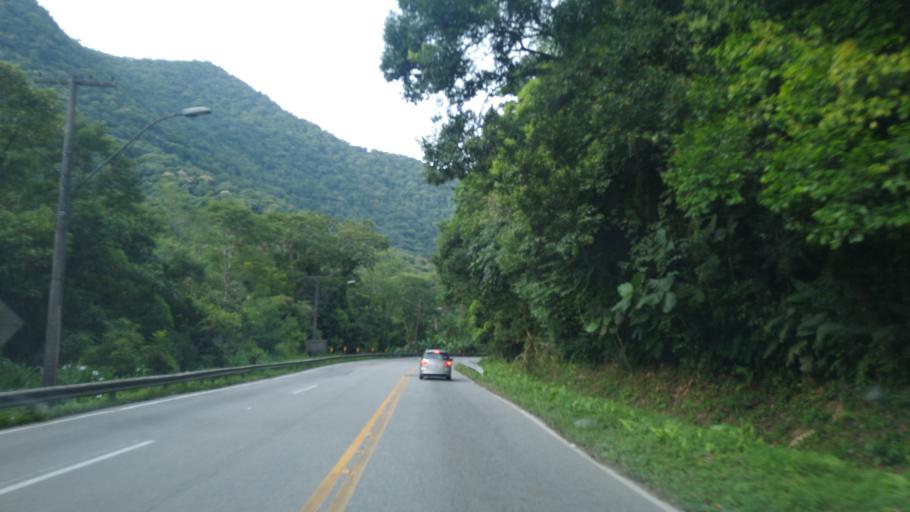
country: BR
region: Santa Catarina
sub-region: Joinville
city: Joinville
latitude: -26.1811
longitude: -49.0155
